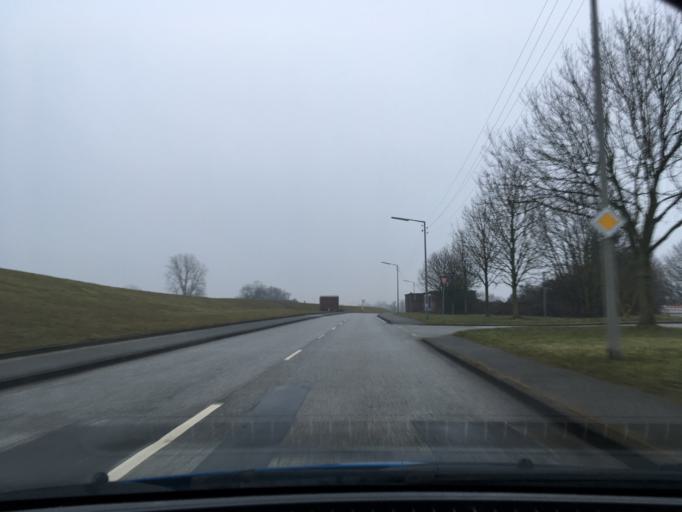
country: DE
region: Hamburg
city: Harburg
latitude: 53.4699
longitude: 9.9975
